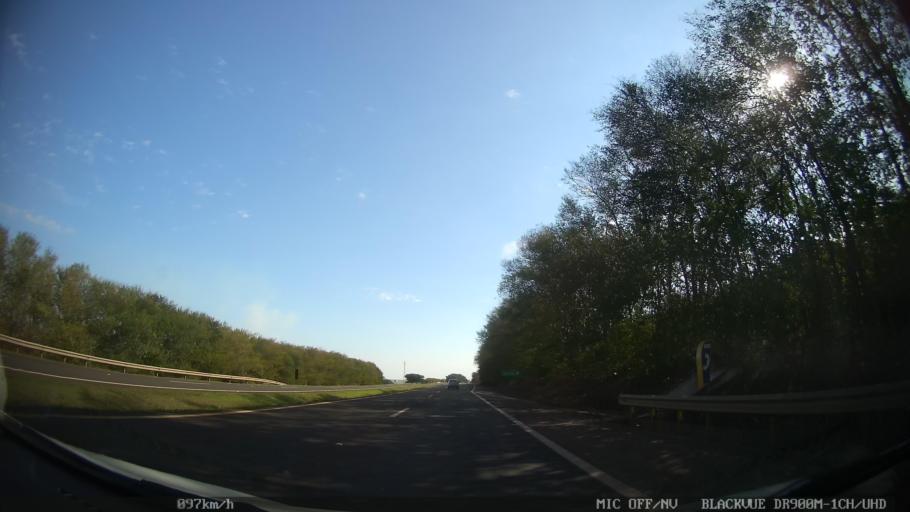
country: BR
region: Sao Paulo
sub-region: Iracemapolis
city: Iracemapolis
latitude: -22.6690
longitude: -47.5434
